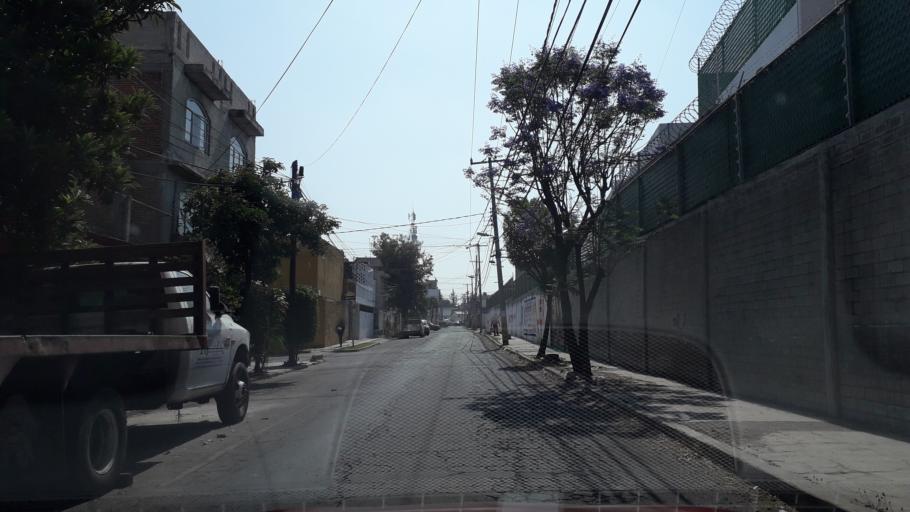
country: MX
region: Puebla
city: Puebla
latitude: 19.0767
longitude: -98.2138
